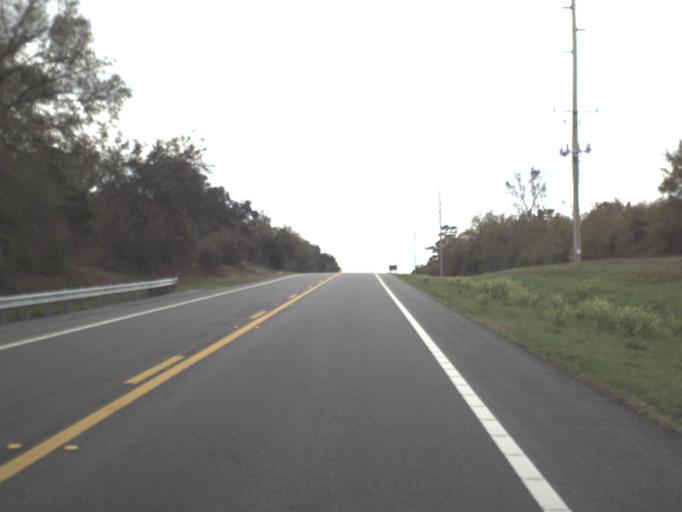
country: US
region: Florida
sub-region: Gadsden County
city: Quincy
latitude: 30.4482
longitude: -84.6439
